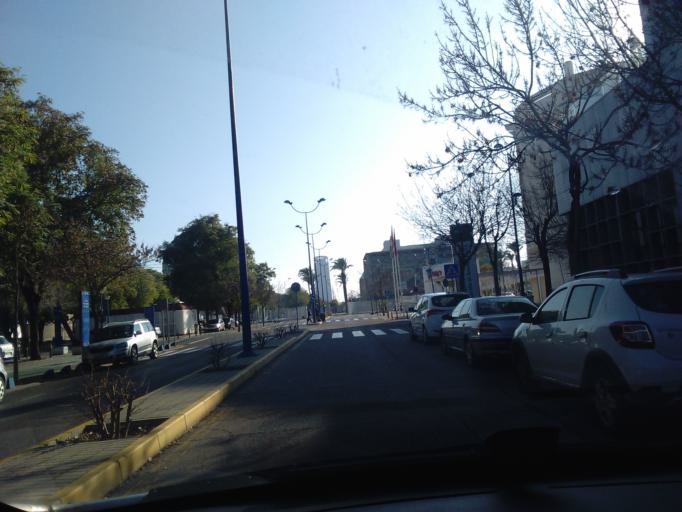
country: ES
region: Andalusia
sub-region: Provincia de Sevilla
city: Camas
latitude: 37.4076
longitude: -6.0064
